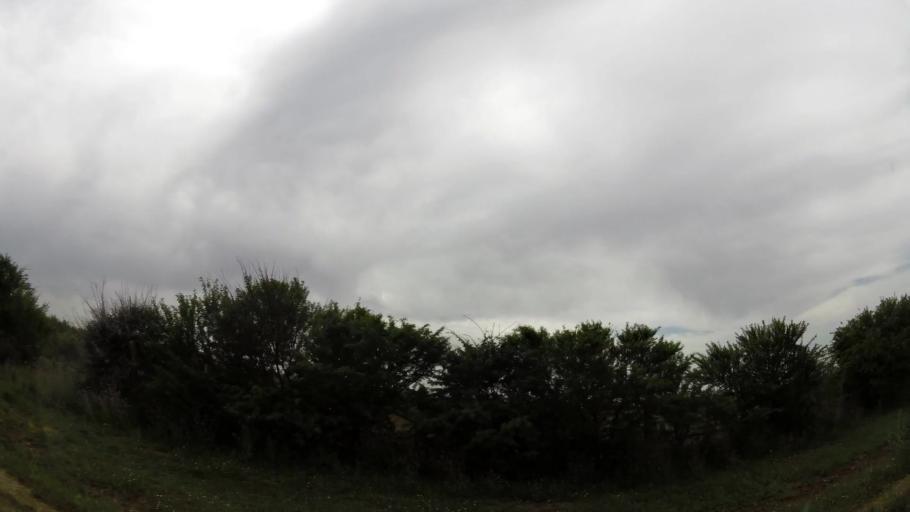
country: MA
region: Rabat-Sale-Zemmour-Zaer
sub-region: Khemisset
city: Tiflet
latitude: 33.8245
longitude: -6.2722
